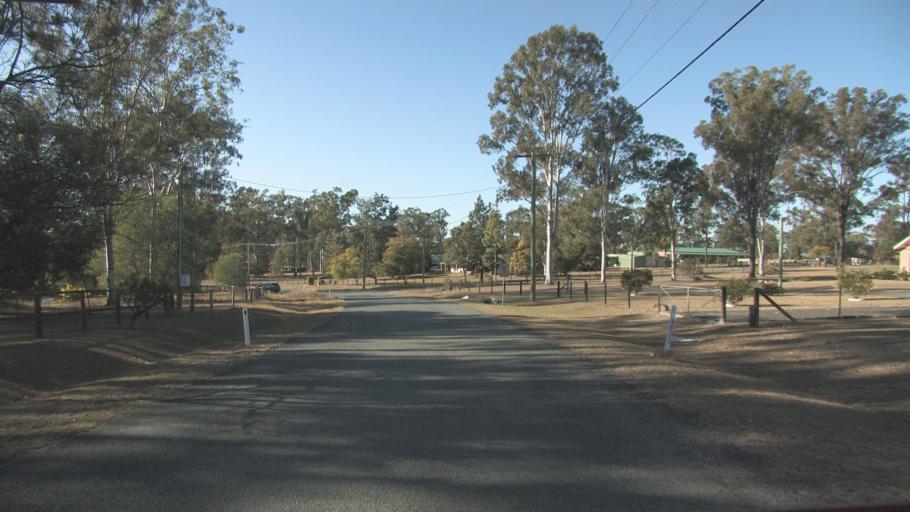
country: AU
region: Queensland
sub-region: Logan
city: Cedar Vale
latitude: -27.8396
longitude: 153.0101
